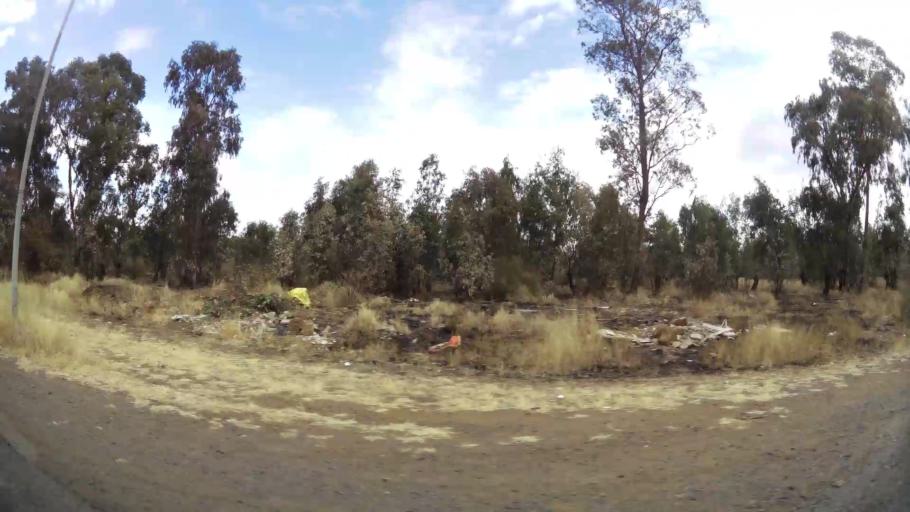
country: ZA
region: Orange Free State
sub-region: Fezile Dabi District Municipality
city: Kroonstad
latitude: -27.6345
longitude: 27.2180
